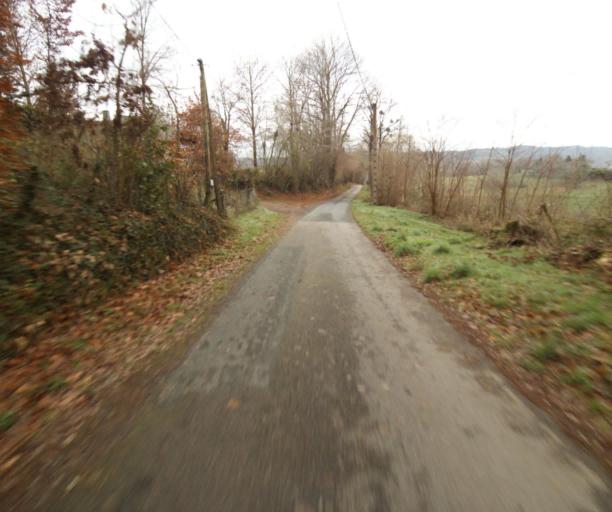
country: FR
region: Limousin
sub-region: Departement de la Correze
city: Laguenne
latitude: 45.2346
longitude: 1.7458
